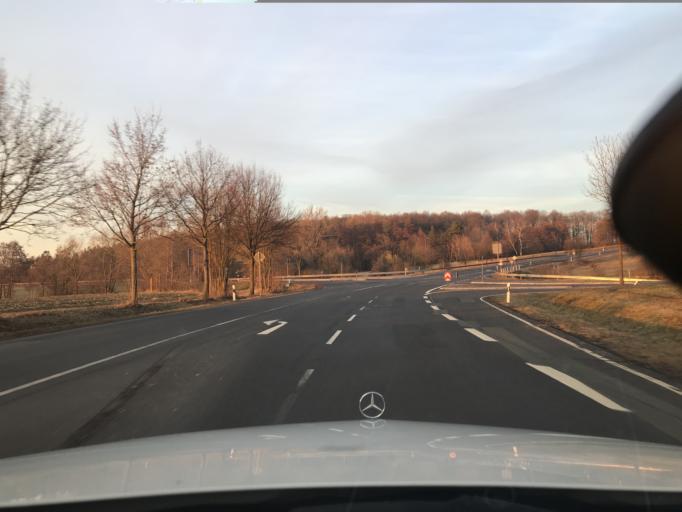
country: DE
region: Thuringia
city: Ernstroda
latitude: 50.8774
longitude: 10.6582
